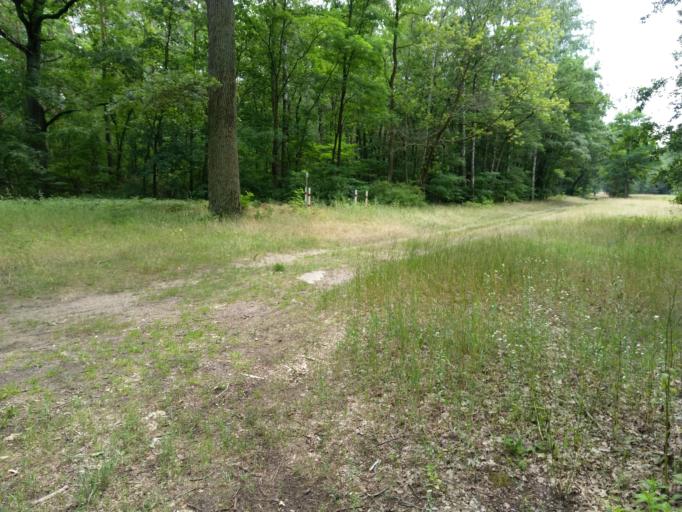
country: DE
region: Berlin
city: Friedrichshagen
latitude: 52.4715
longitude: 13.6521
